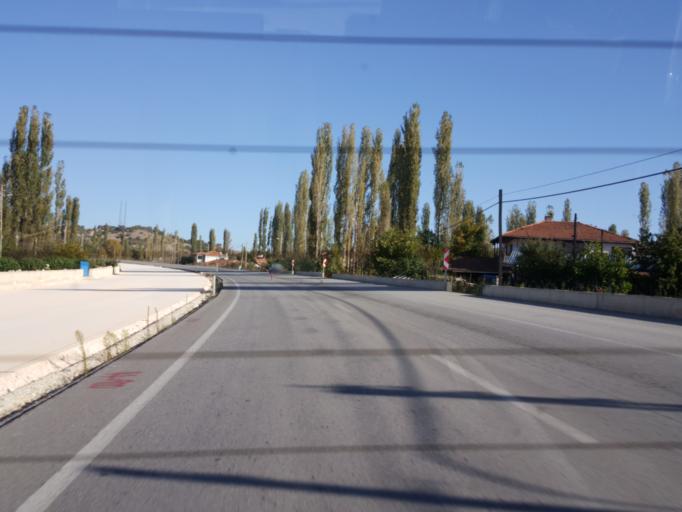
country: TR
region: Amasya
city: Ezinepazari
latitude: 40.5457
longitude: 36.1520
